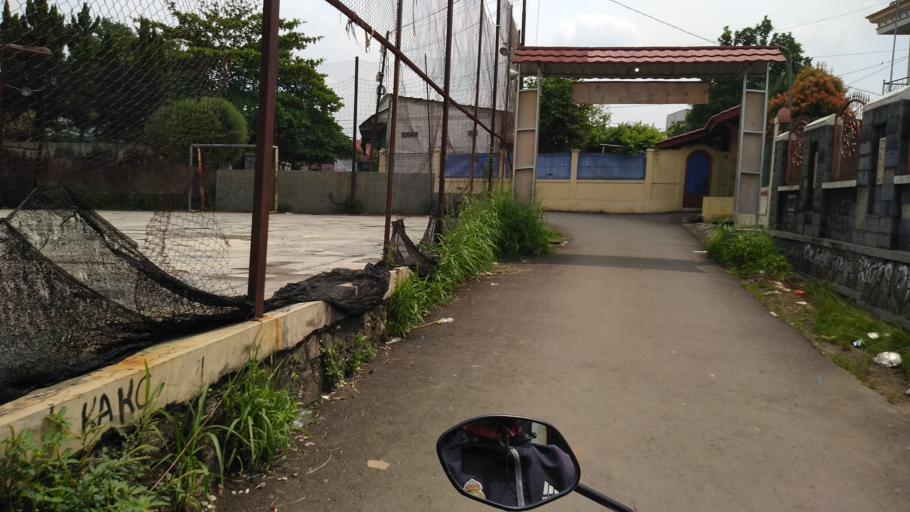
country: ID
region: West Java
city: Ciampea
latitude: -6.5592
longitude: 106.7468
